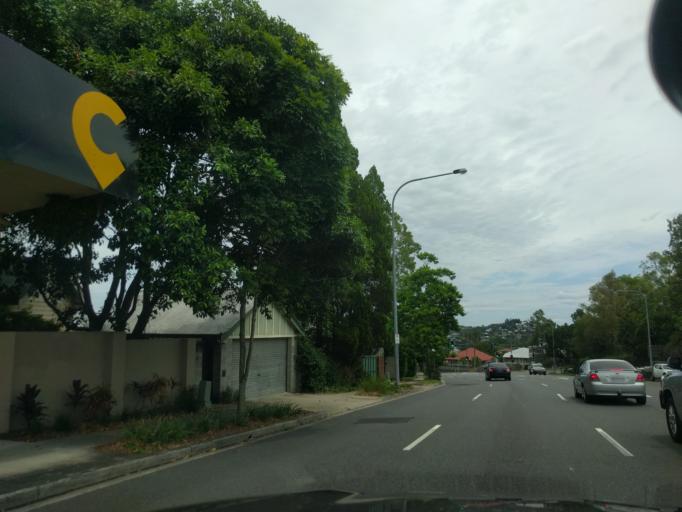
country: AU
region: Queensland
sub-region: Brisbane
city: Spring Hill
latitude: -27.4503
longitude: 153.0110
